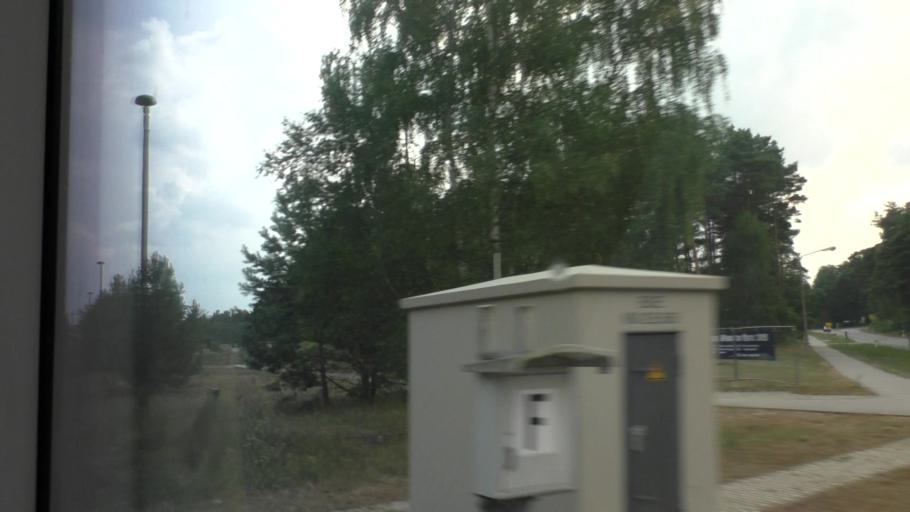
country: DE
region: Brandenburg
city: Wendisch Rietz
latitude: 52.2096
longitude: 14.0066
